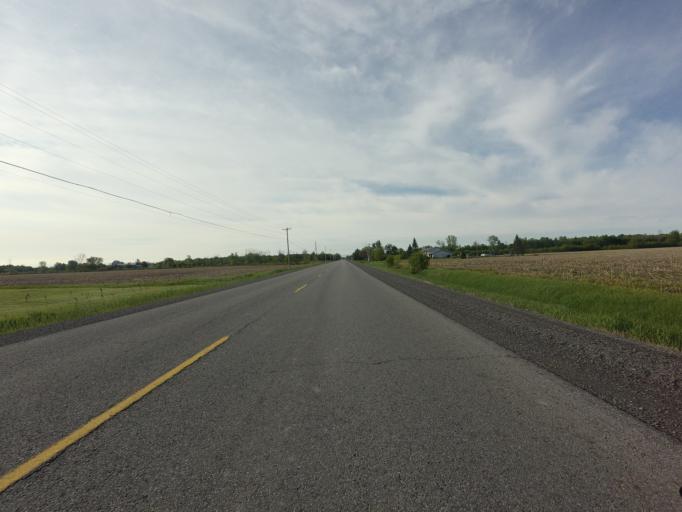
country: CA
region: Ontario
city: Ottawa
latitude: 45.2971
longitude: -75.4520
